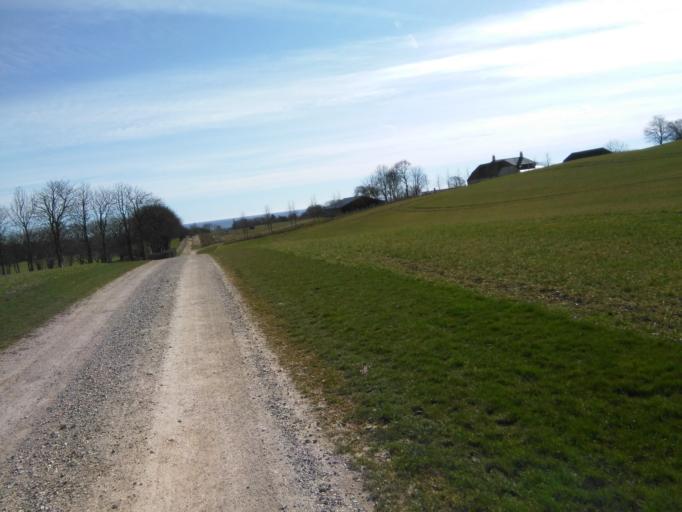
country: DK
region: Central Jutland
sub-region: Arhus Kommune
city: Beder
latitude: 56.0499
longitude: 10.2482
